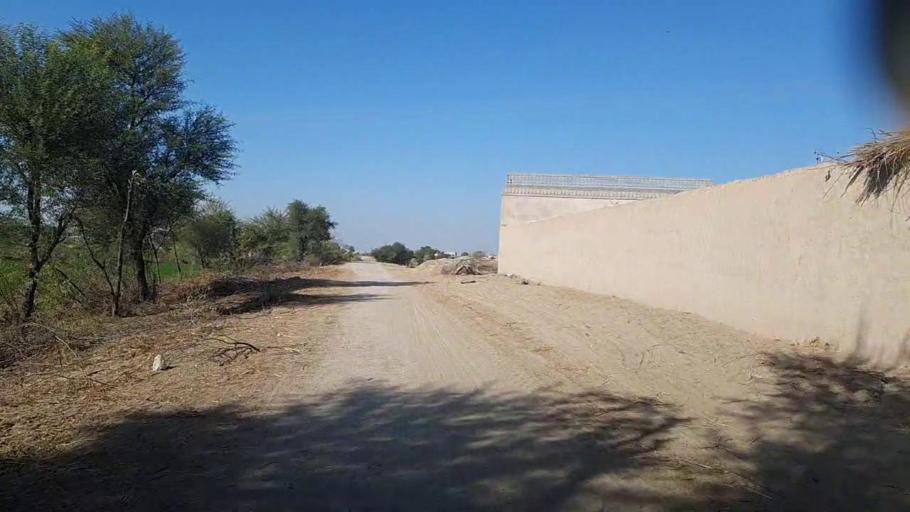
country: PK
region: Sindh
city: Khairpur
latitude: 27.9187
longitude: 69.7516
